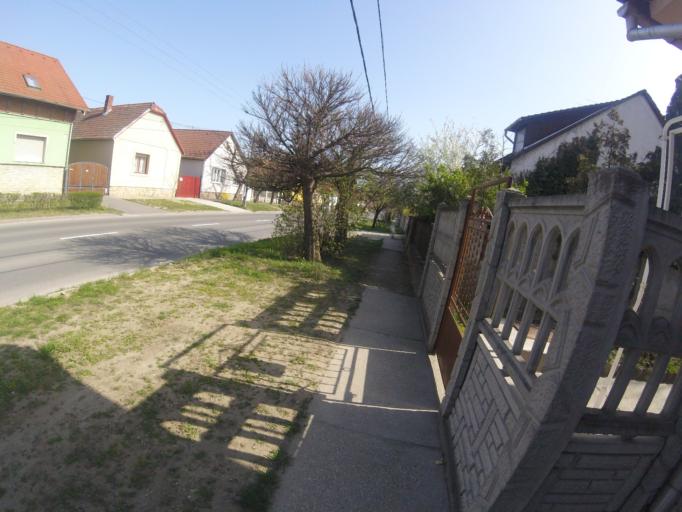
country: HU
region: Pest
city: Pilisvorosvar
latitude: 47.6232
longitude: 18.9003
